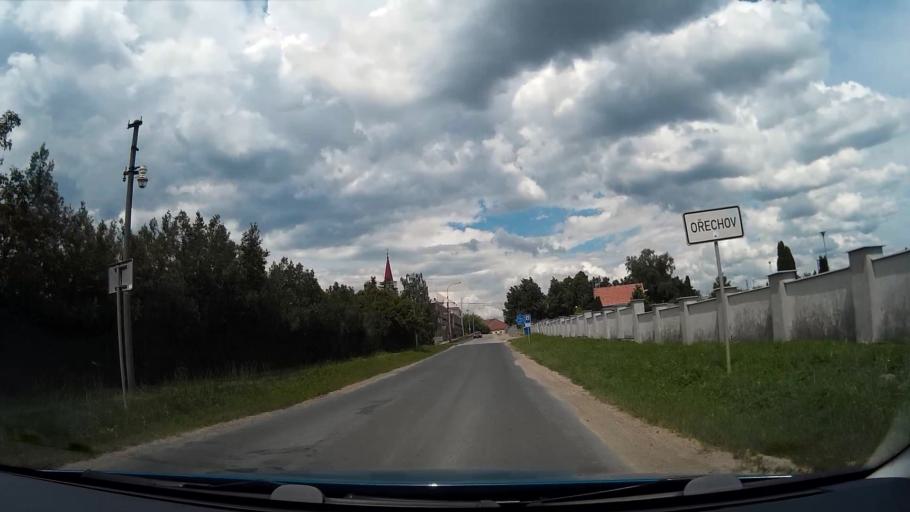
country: CZ
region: South Moravian
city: Orechov
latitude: 49.1082
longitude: 16.5263
